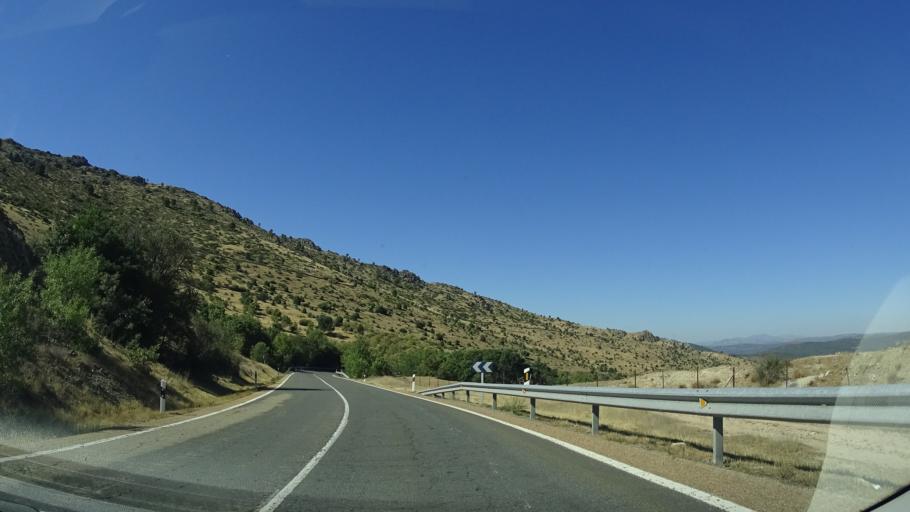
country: ES
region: Madrid
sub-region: Provincia de Madrid
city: Zarzalejo
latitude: 40.5625
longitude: -4.2191
